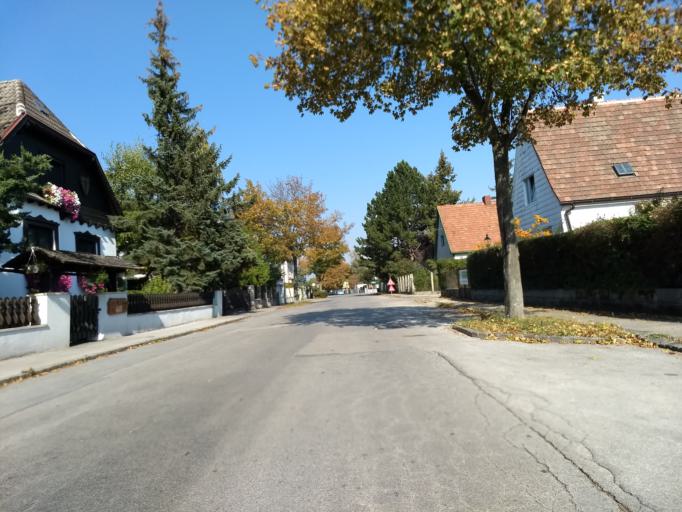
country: AT
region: Lower Austria
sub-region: Politischer Bezirk Modling
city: Brunn am Gebirge
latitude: 48.1103
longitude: 16.2804
